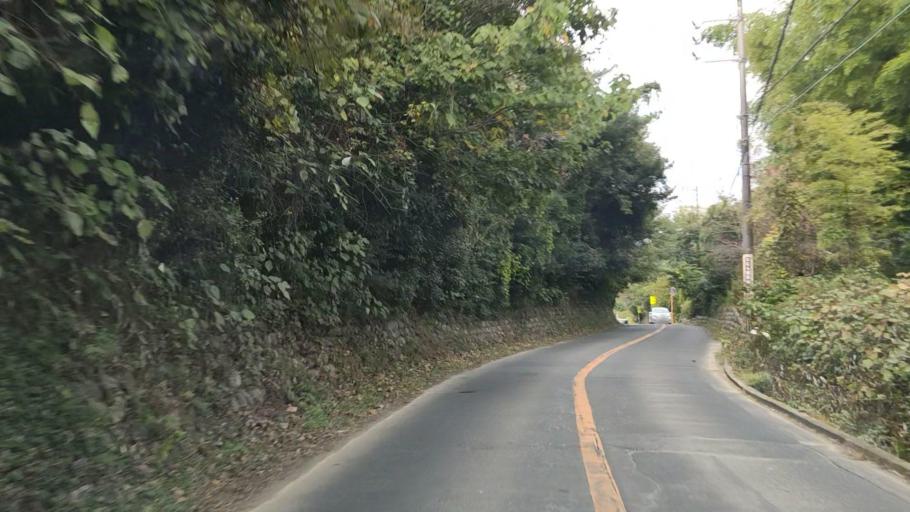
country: JP
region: Shizuoka
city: Shizuoka-shi
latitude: 34.9898
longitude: 138.4551
